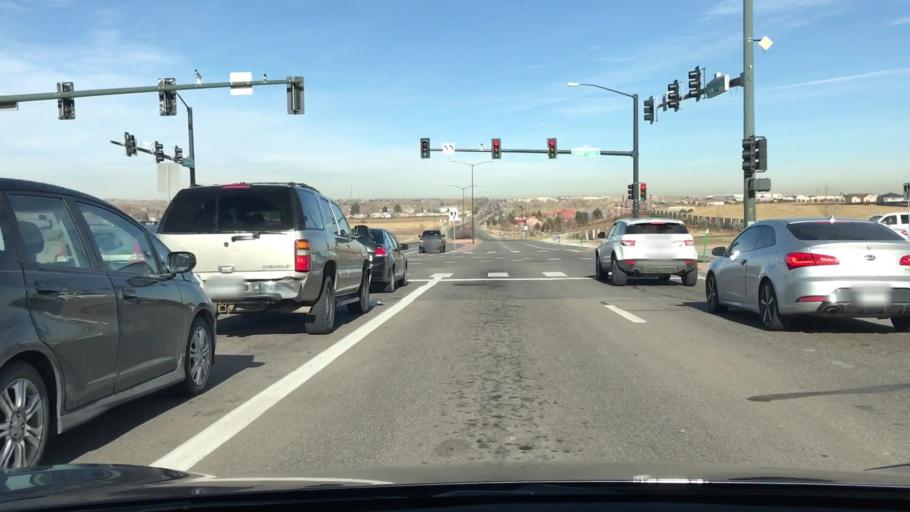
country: US
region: Colorado
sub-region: Adams County
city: Northglenn
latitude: 39.9282
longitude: -104.9967
